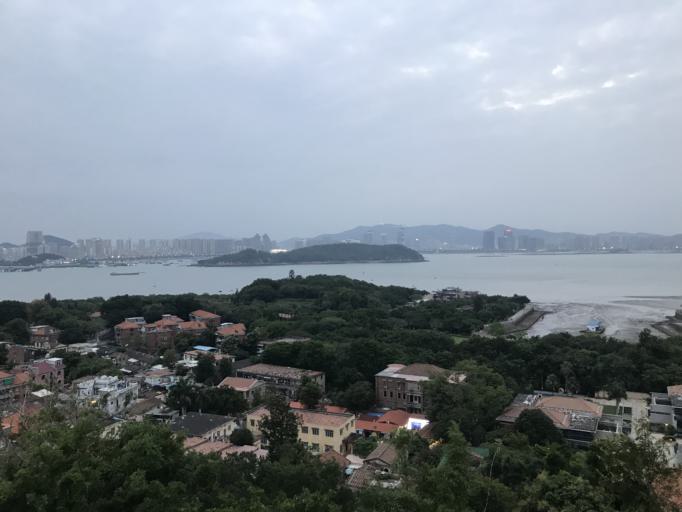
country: CN
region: Fujian
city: Xiamen
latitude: 24.4503
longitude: 118.0606
